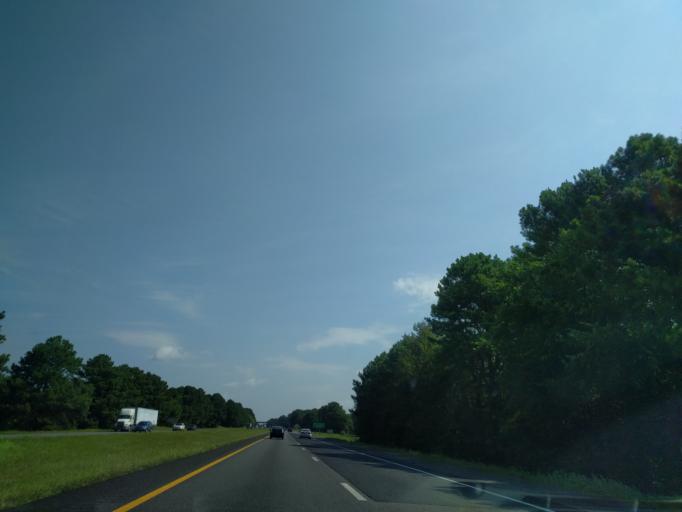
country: US
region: Tennessee
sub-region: Sumner County
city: Portland
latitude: 36.5973
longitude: -86.5922
